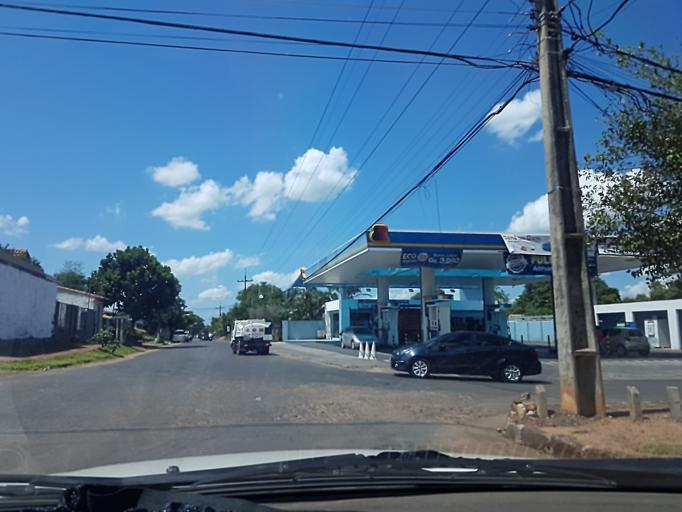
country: PY
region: Central
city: San Lorenzo
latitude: -25.2582
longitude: -57.4945
